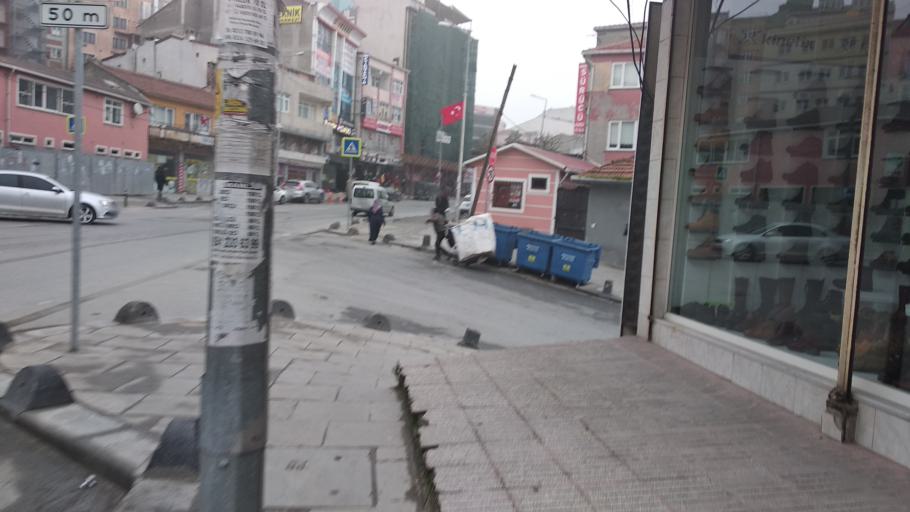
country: TR
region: Istanbul
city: Basaksehir
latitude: 41.1840
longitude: 28.7397
